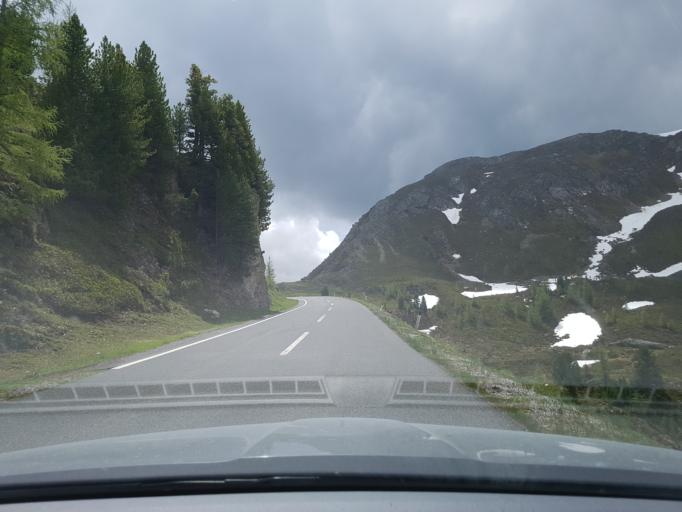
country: AT
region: Carinthia
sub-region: Politischer Bezirk Spittal an der Drau
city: Kleinkirchheim
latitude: 46.8926
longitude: 13.7922
